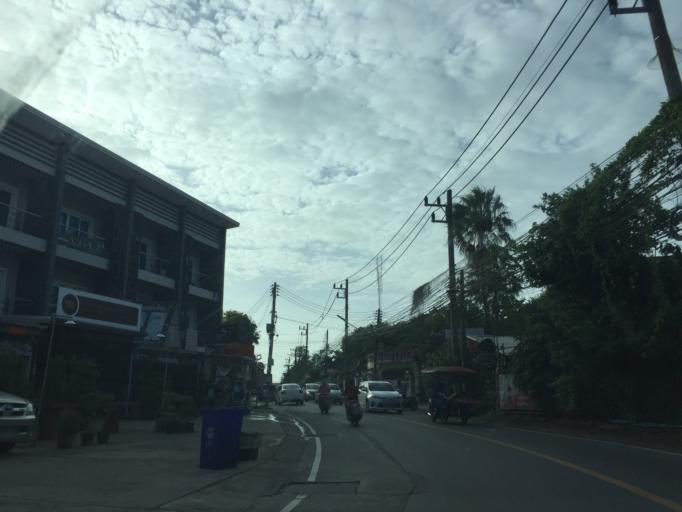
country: TH
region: Phuket
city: Mueang Phuket
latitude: 7.8622
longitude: 98.3709
